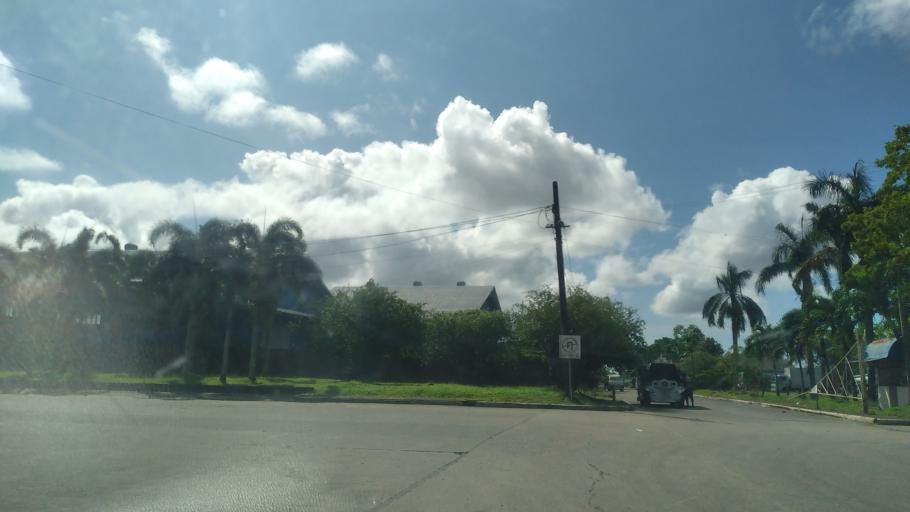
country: PH
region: Calabarzon
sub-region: Province of Quezon
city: Lucena
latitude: 13.9576
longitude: 121.6178
